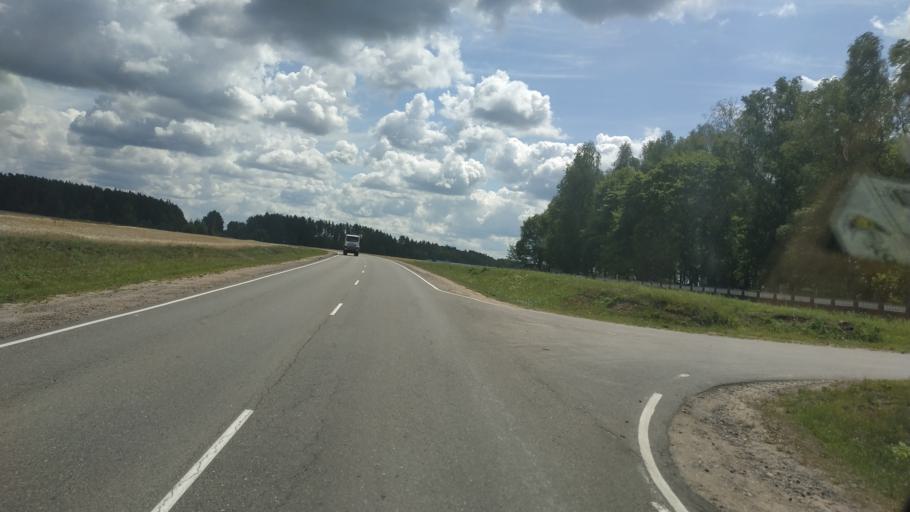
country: BY
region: Mogilev
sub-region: Mahilyowski Rayon
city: Veyno
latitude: 53.8334
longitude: 30.4023
